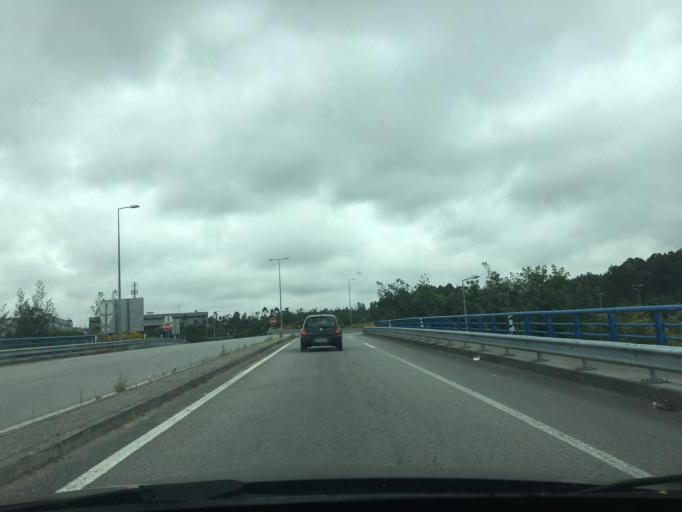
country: PT
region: Porto
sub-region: Matosinhos
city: Santa Cruz do Bispo
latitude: 41.2235
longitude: -8.6653
